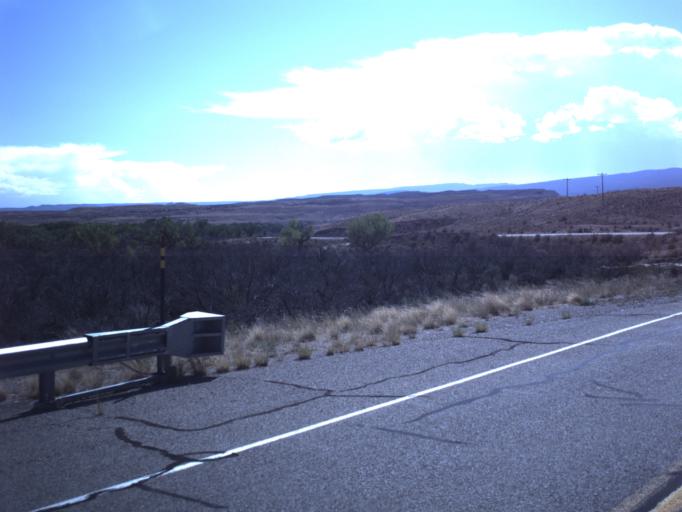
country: US
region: Utah
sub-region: Grand County
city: Moab
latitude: 38.8611
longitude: -109.2943
